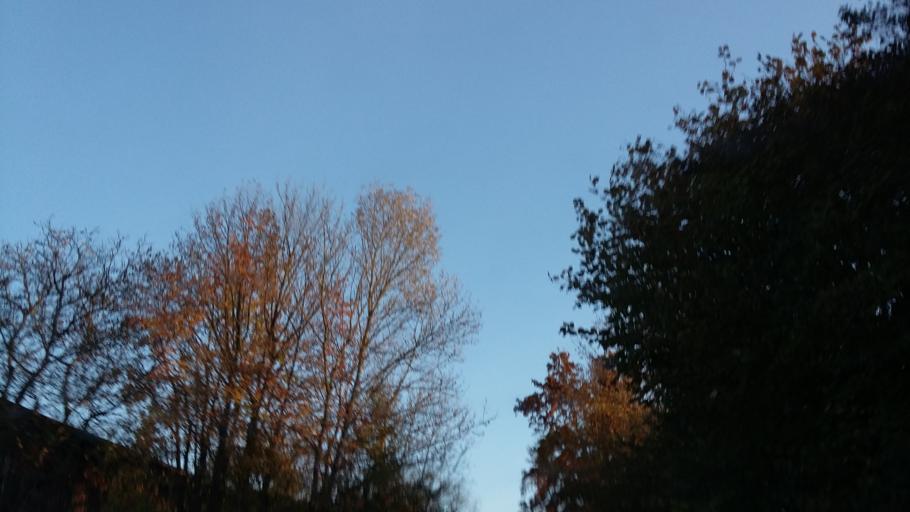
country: DE
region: Bavaria
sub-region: Upper Bavaria
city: Gstadt am Chiemsee
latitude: 47.8889
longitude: 12.4017
